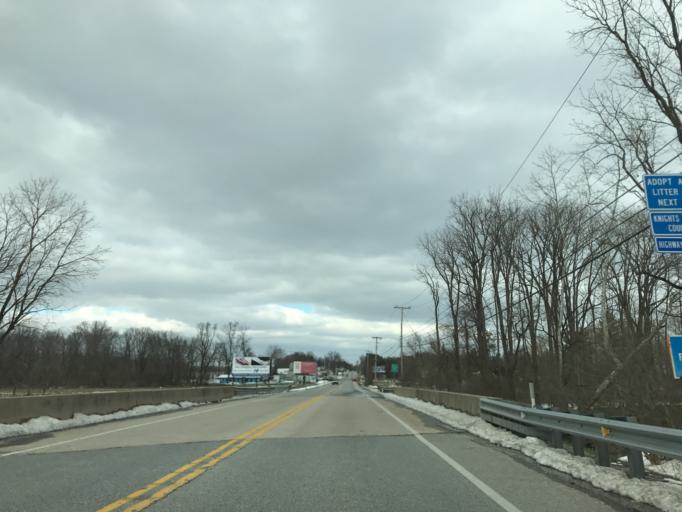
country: US
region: Pennsylvania
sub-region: York County
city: Spring Grove
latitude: 39.8484
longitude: -76.8968
